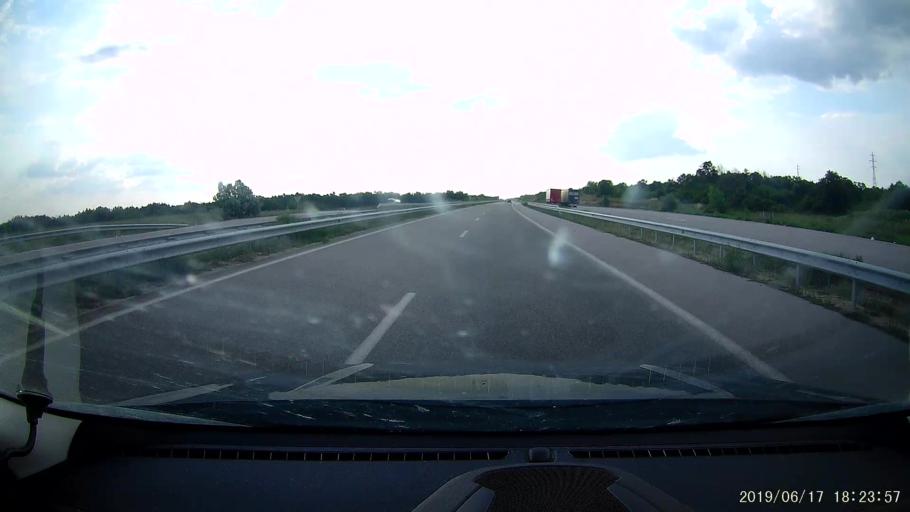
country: BG
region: Khaskovo
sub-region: Obshtina Dimitrovgrad
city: Dimitrovgrad
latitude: 41.9791
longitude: 25.7055
